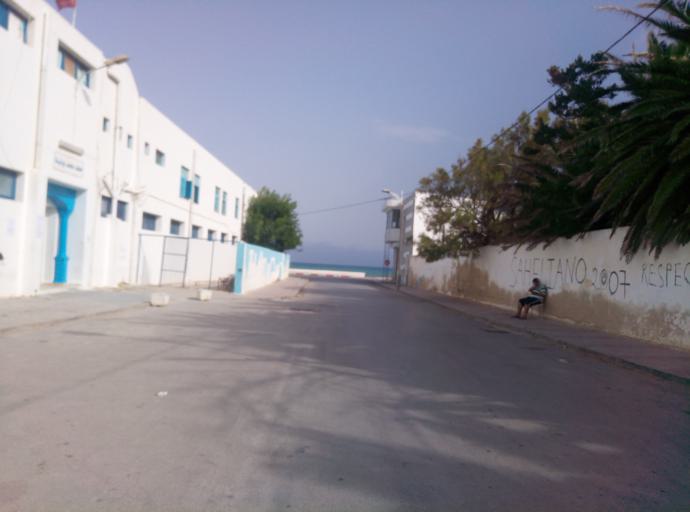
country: TN
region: Nabul
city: Al Hammamat
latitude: 36.3942
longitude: 10.6178
